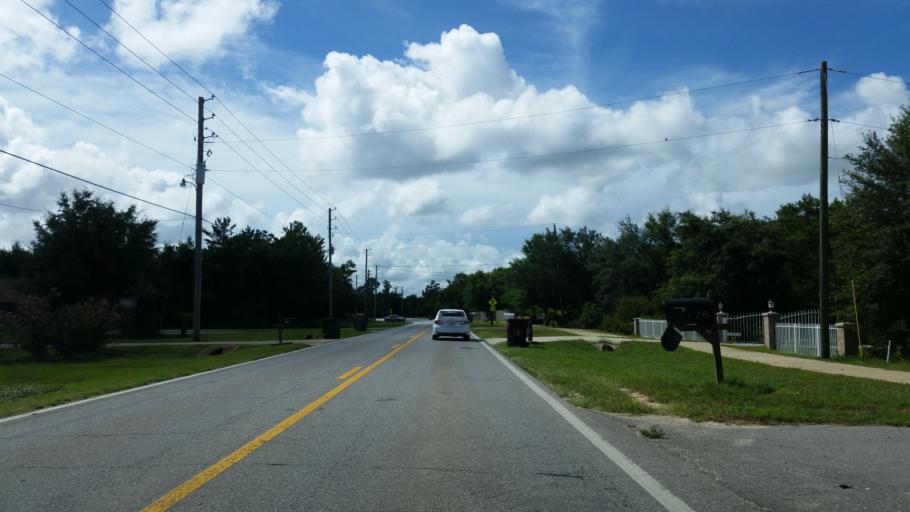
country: US
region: Florida
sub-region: Santa Rosa County
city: Holley
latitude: 30.4436
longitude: -86.9244
